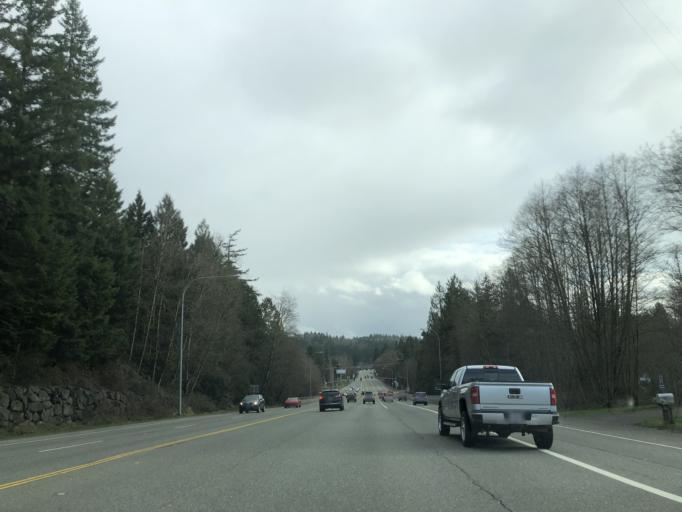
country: US
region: Washington
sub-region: Kitsap County
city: Poulsbo
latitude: 47.7538
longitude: -122.6482
